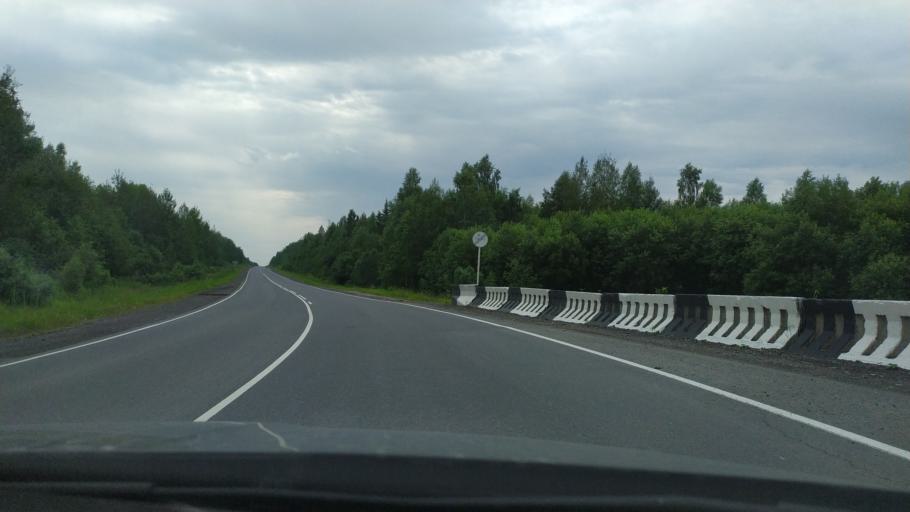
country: RU
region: Perm
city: Chusovoy
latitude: 58.4083
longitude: 57.8739
